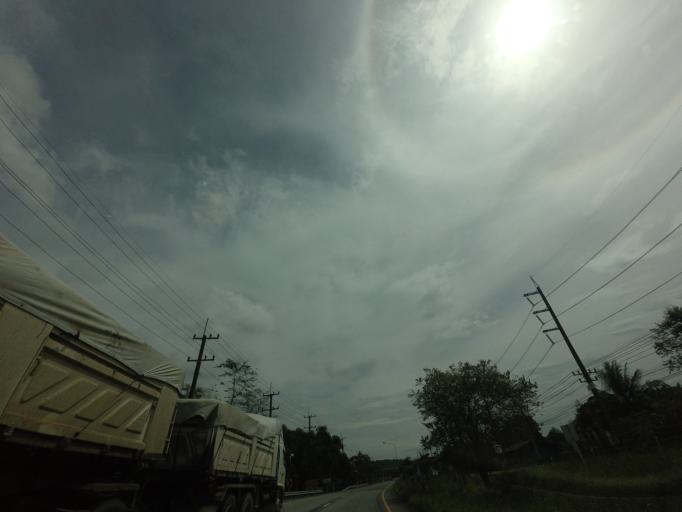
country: TH
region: Rayong
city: Klaeng
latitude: 12.7124
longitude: 101.5585
